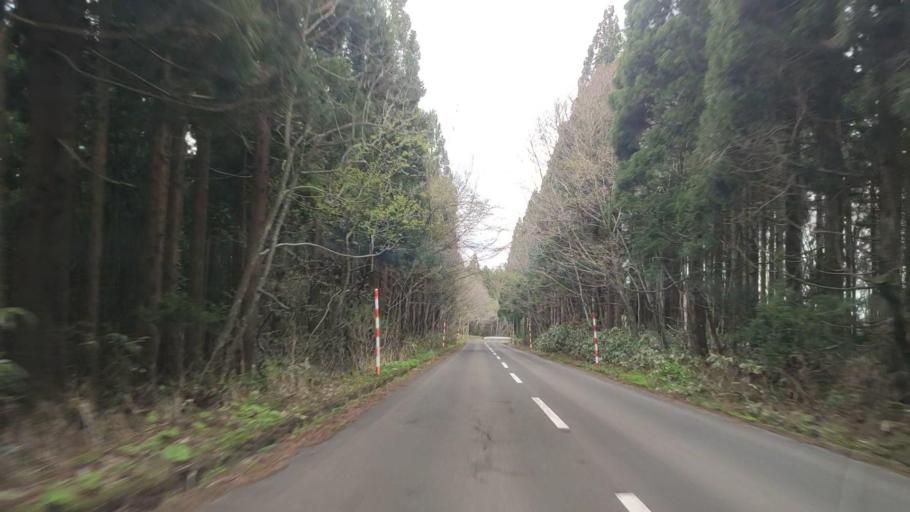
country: JP
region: Akita
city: Hanawa
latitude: 40.3920
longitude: 140.7951
